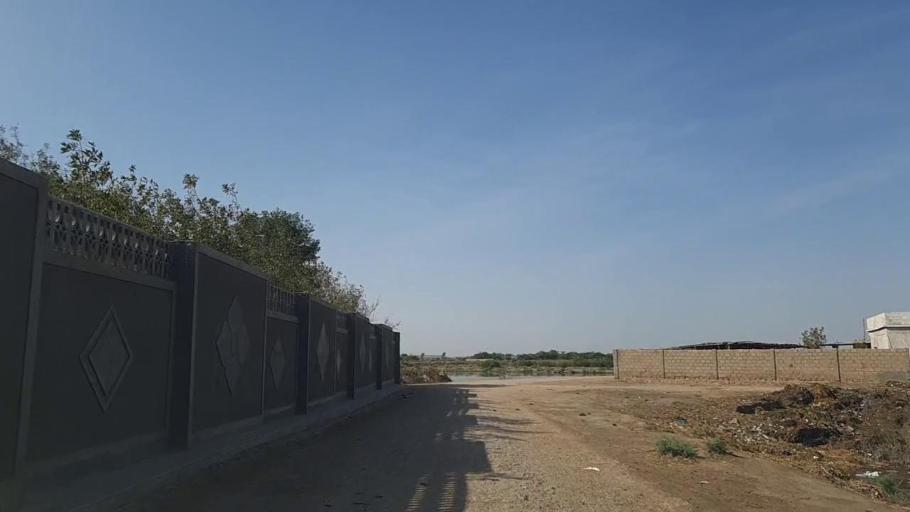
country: PK
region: Sindh
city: Thatta
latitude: 24.5935
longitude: 67.8847
